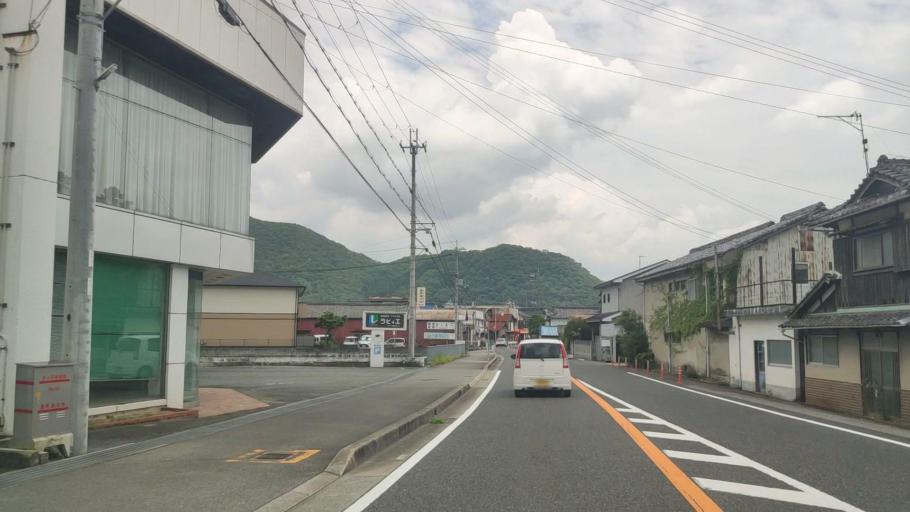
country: JP
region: Hyogo
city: Tatsunocho-tominaga
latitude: 34.9207
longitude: 134.5438
